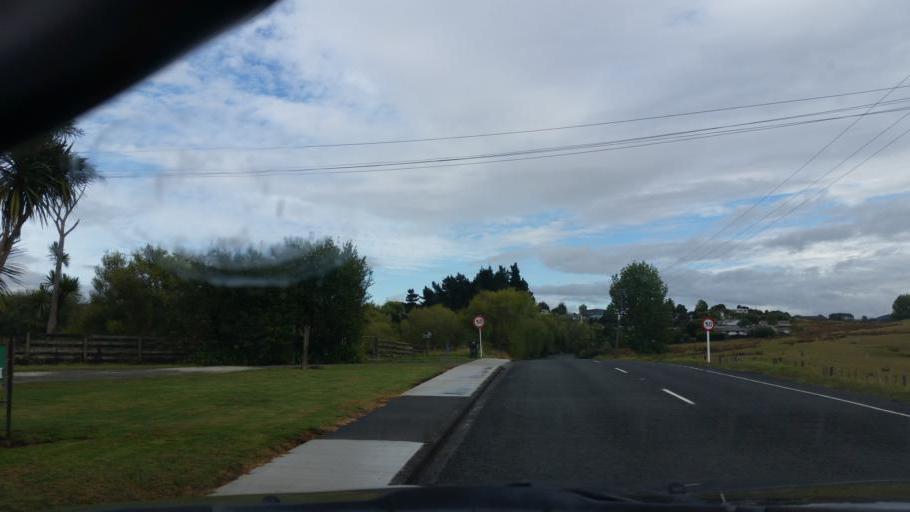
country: NZ
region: Northland
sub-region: Whangarei
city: Ruakaka
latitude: -36.1119
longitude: 174.3638
